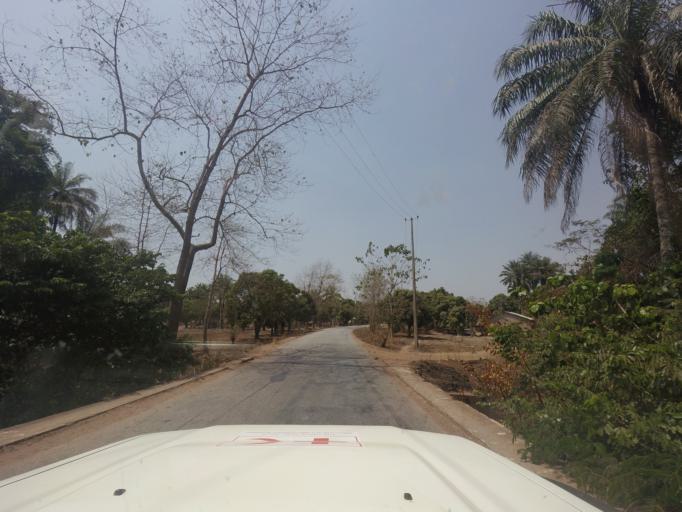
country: GN
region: Kindia
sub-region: Kindia
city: Kindia
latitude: 9.9258
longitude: -12.9914
